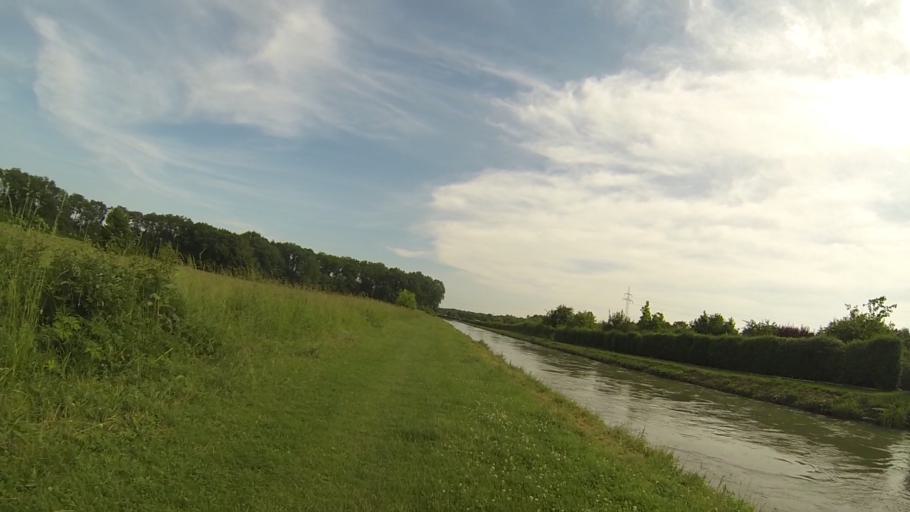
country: DE
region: Baden-Wuerttemberg
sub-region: Tuebingen Region
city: Ulm
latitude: 48.3790
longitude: 9.9951
